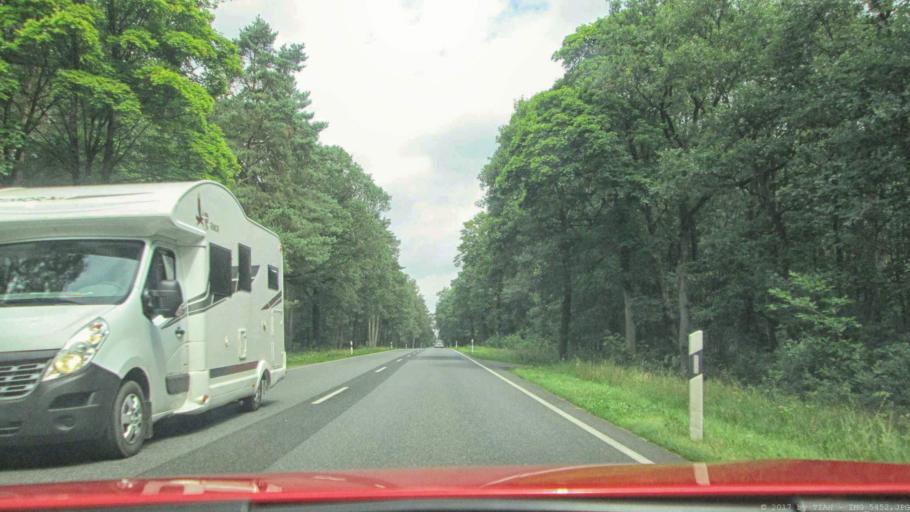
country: DE
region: Lower Saxony
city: Dedelstorf
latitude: 52.7179
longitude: 10.4815
